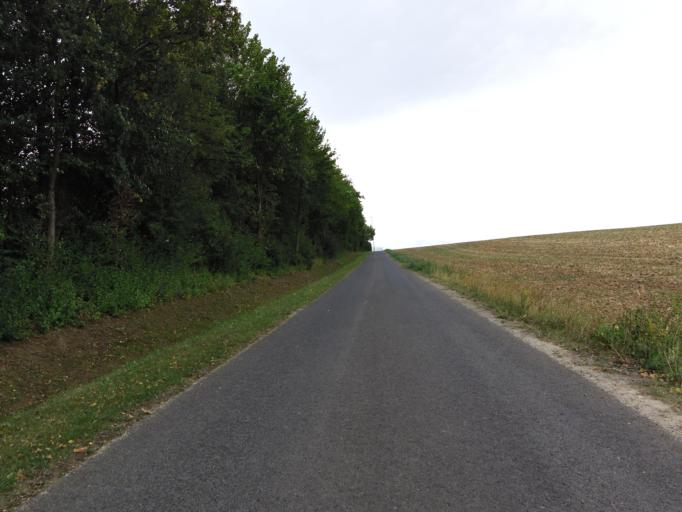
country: DE
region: Bavaria
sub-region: Regierungsbezirk Unterfranken
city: Rimpar
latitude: 49.8419
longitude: 9.9464
